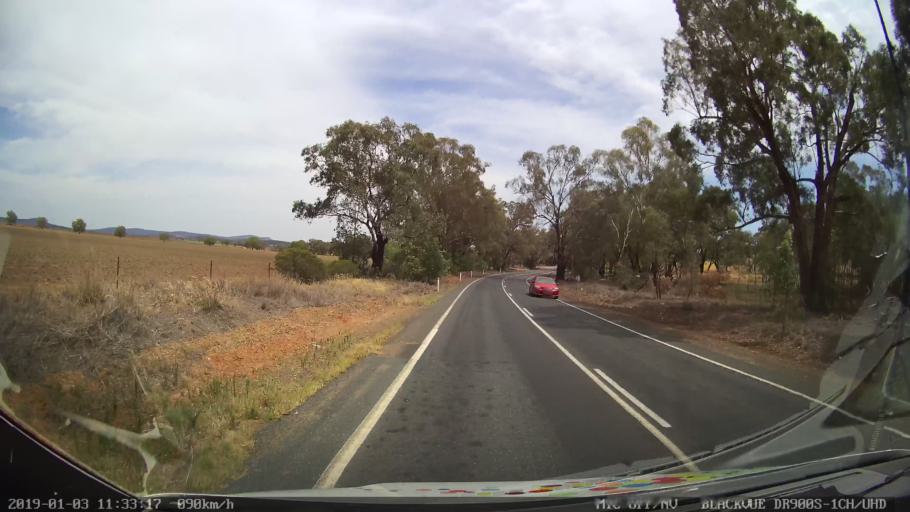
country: AU
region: New South Wales
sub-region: Weddin
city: Grenfell
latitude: -33.9486
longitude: 148.1722
